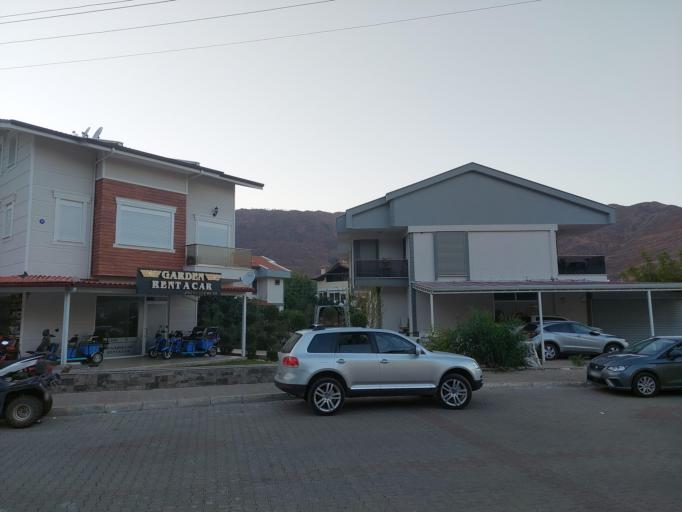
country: TR
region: Mugla
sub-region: Marmaris
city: Marmaris
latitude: 36.7969
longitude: 28.2256
